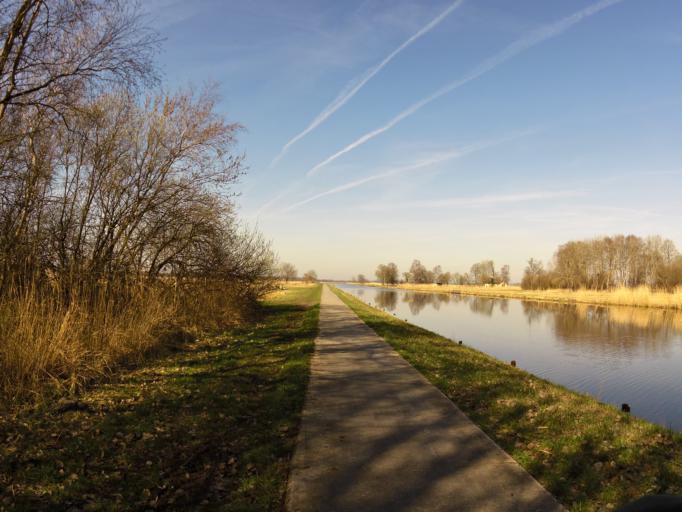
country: NL
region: Overijssel
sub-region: Gemeente Steenwijkerland
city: Oldemarkt
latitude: 52.7990
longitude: 5.9626
